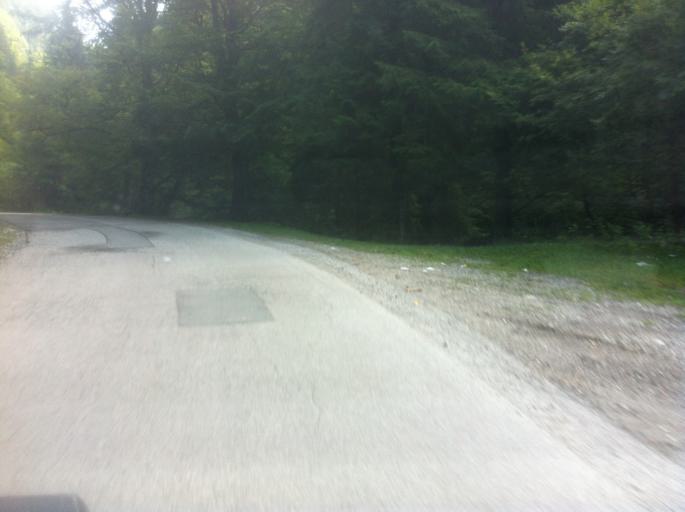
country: RO
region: Hunedoara
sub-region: Oras Petrila
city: Petrila
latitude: 45.4064
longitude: 23.5077
